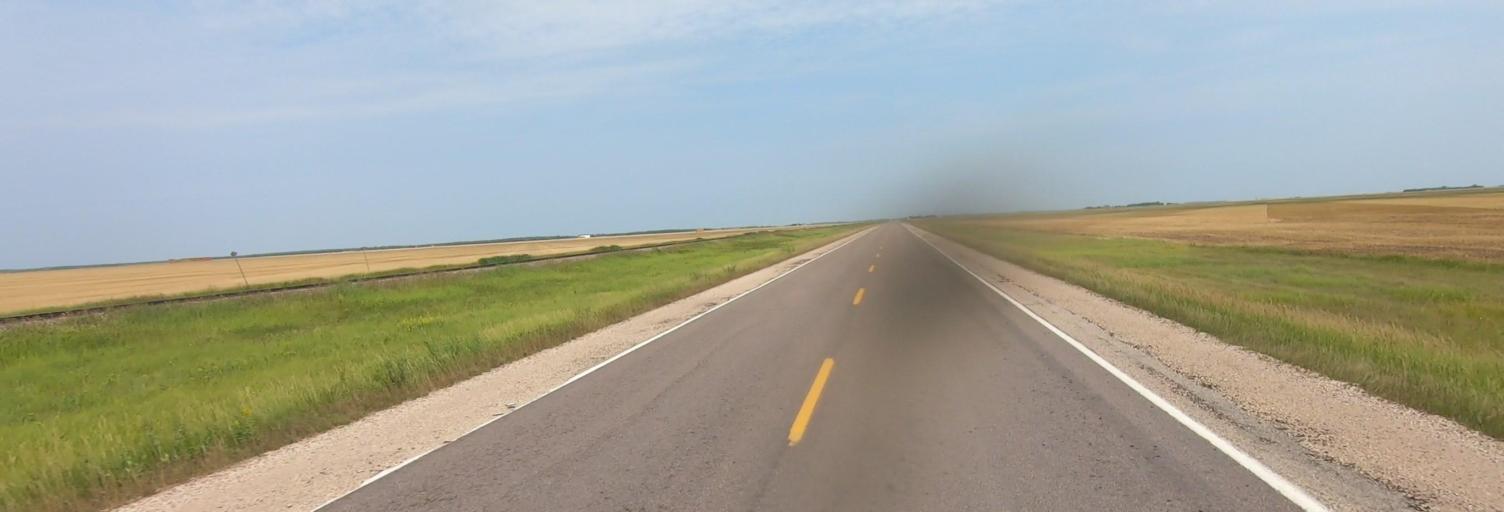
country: CA
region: Manitoba
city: Headingley
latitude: 49.6236
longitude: -97.3143
